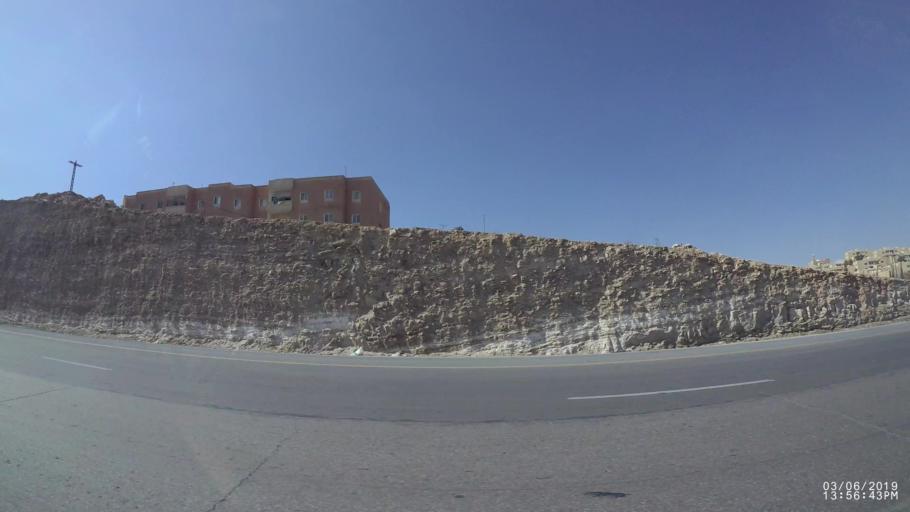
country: JO
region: Zarqa
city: Zarqa
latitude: 32.0398
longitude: 36.1060
